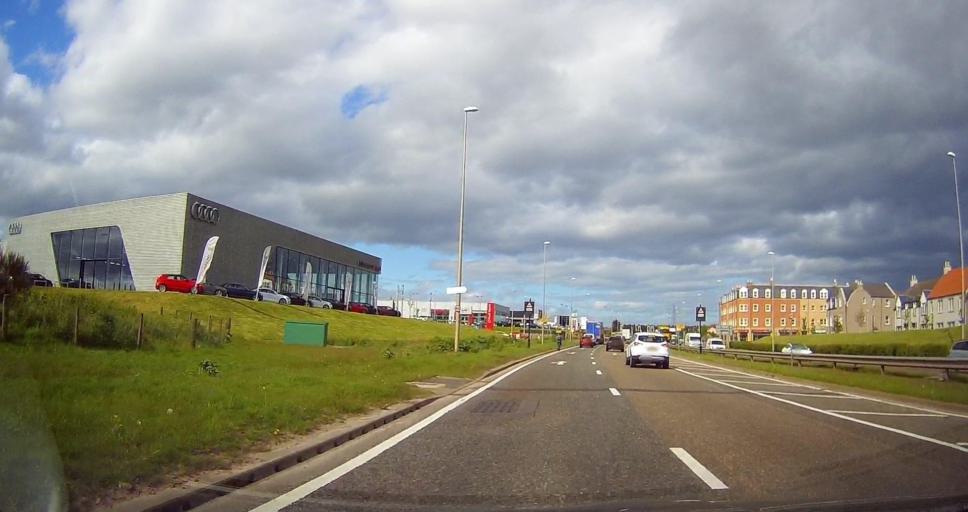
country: GB
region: Scotland
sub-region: Aberdeen City
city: Aberdeen
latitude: 57.1041
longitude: -2.0968
